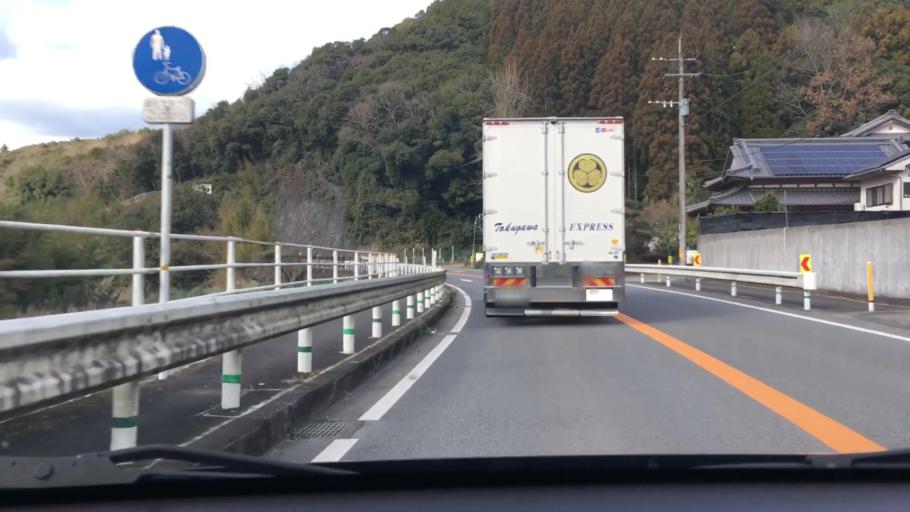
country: JP
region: Oita
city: Usuki
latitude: 33.0091
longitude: 131.7077
